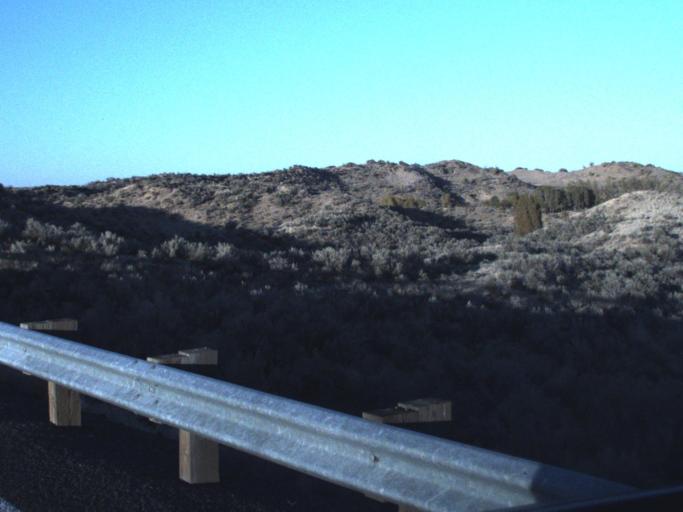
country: US
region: Washington
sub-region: Franklin County
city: Connell
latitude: 46.7727
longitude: -118.5476
